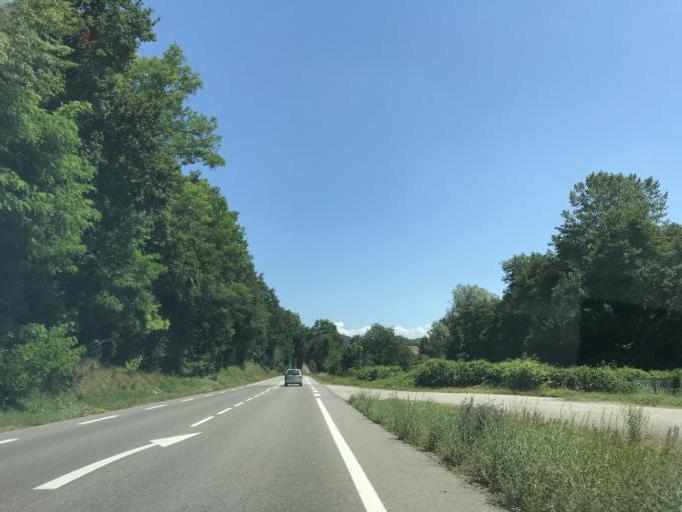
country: FR
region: Rhone-Alpes
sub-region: Departement de l'Ain
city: Virieu-le-Grand
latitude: 45.8127
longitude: 5.6642
